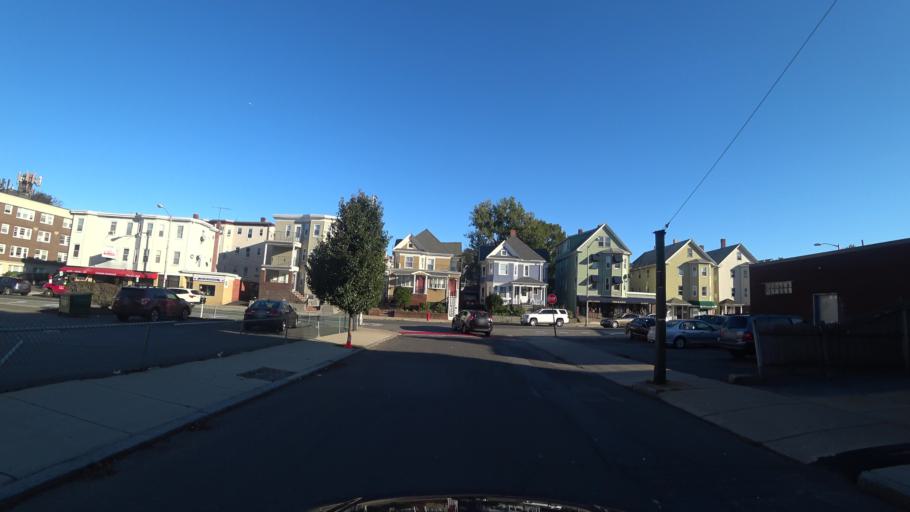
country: US
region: Massachusetts
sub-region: Middlesex County
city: Everett
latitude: 42.4128
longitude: -71.0508
